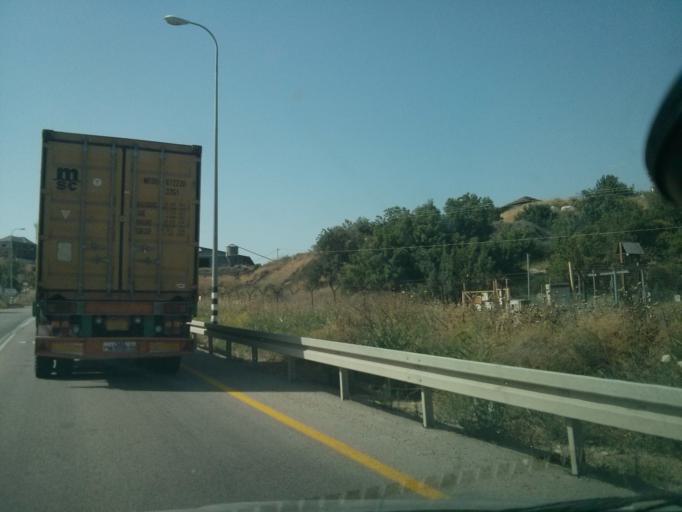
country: IL
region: Jerusalem
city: Bet Shemesh
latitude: 31.6761
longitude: 35.0056
